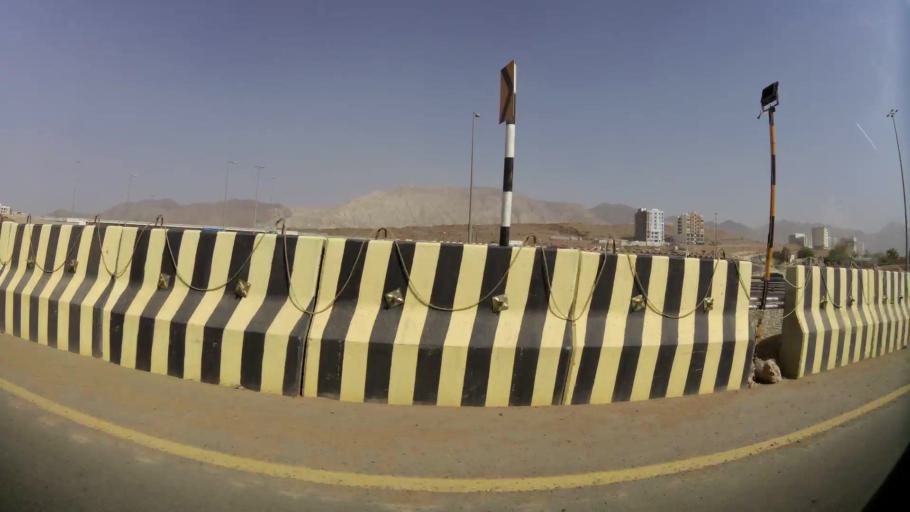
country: OM
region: Muhafazat Masqat
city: Bawshar
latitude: 23.5700
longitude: 58.4054
